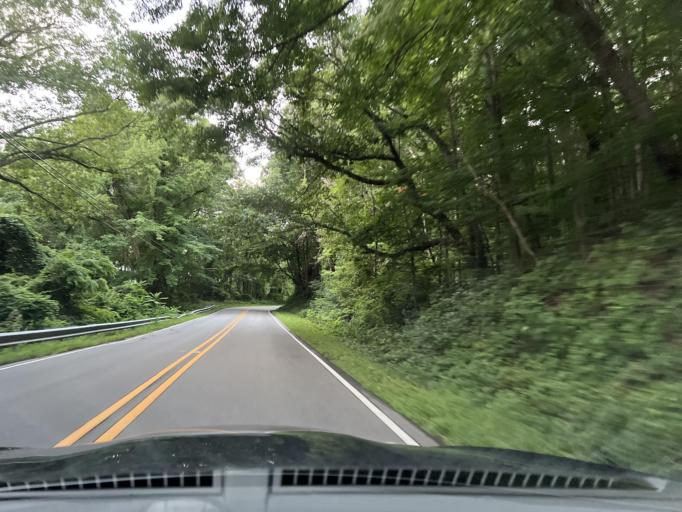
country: US
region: North Carolina
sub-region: Buncombe County
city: Asheville
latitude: 35.6175
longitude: -82.5309
